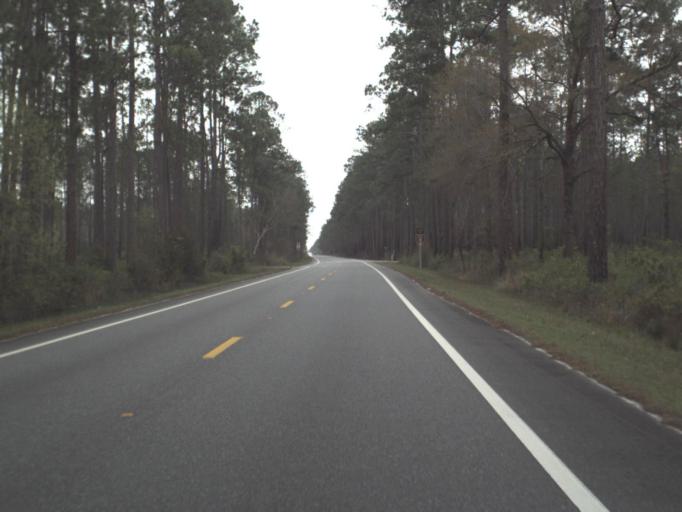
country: US
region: Florida
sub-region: Franklin County
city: Apalachicola
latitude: 29.9640
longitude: -84.9759
